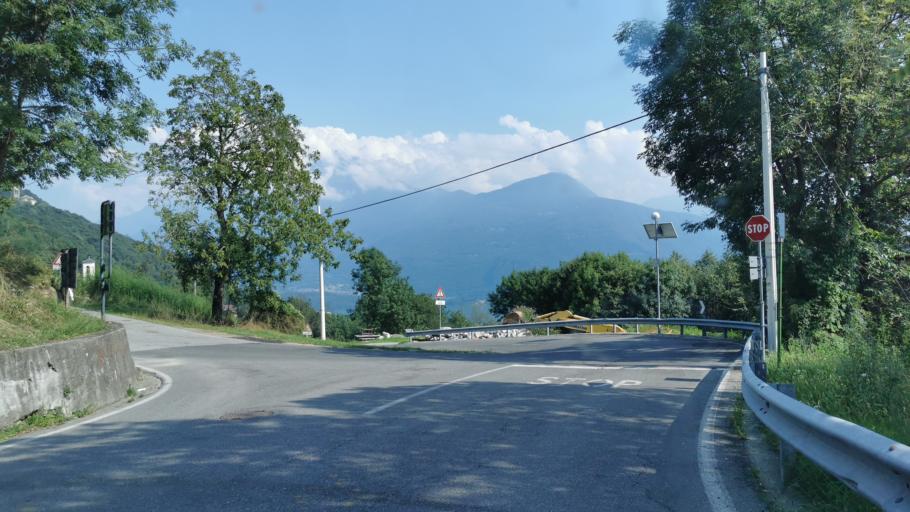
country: IT
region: Lombardy
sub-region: Provincia di Como
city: Dosso del Liro
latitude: 46.1599
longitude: 9.2834
